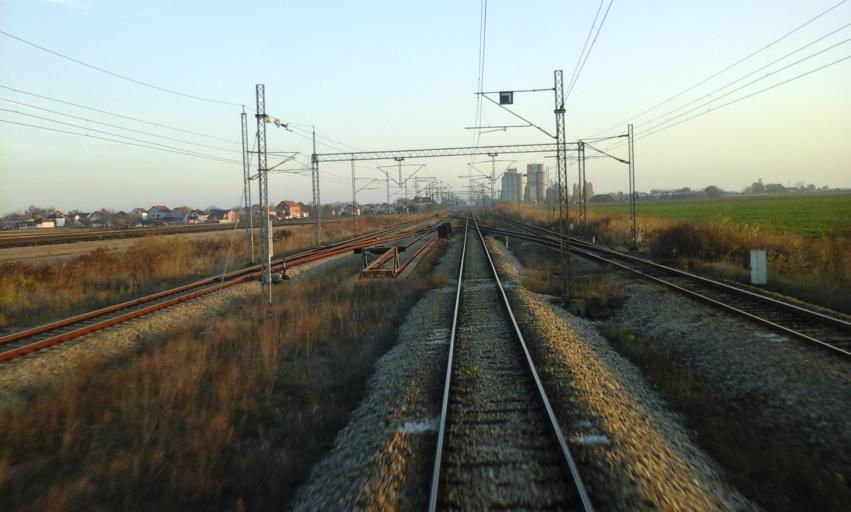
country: RS
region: Autonomna Pokrajina Vojvodina
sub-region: Sremski Okrug
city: Stara Pazova
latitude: 44.9952
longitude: 20.1312
